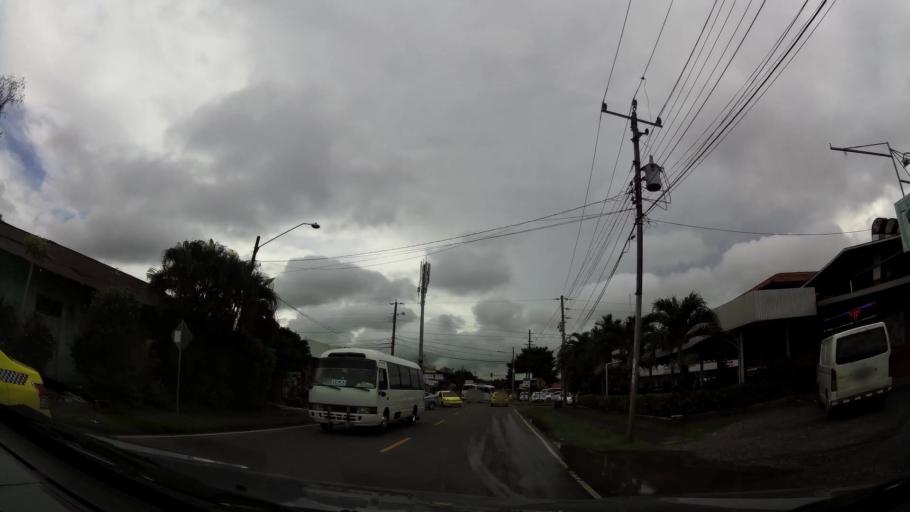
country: PA
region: Chiriqui
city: David
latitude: 8.4229
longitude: -82.4308
